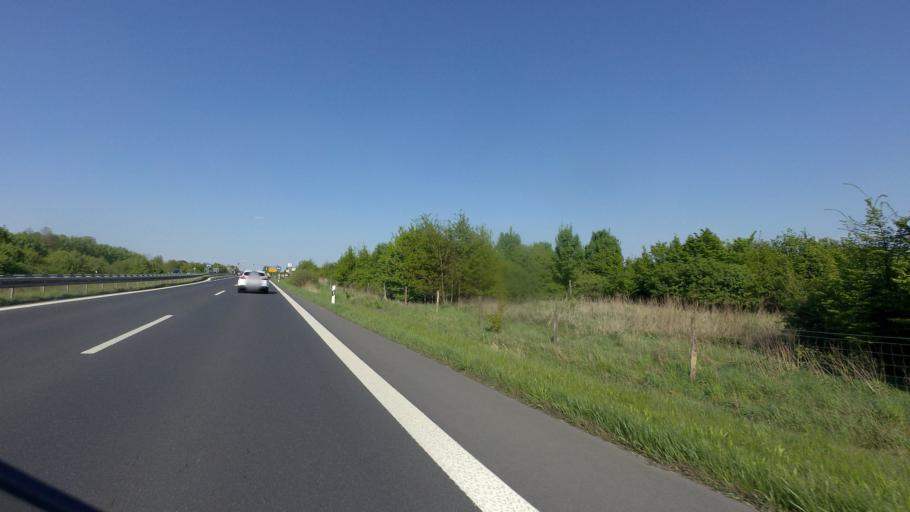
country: DE
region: Berlin
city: Marienfelde
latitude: 52.3891
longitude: 13.3385
